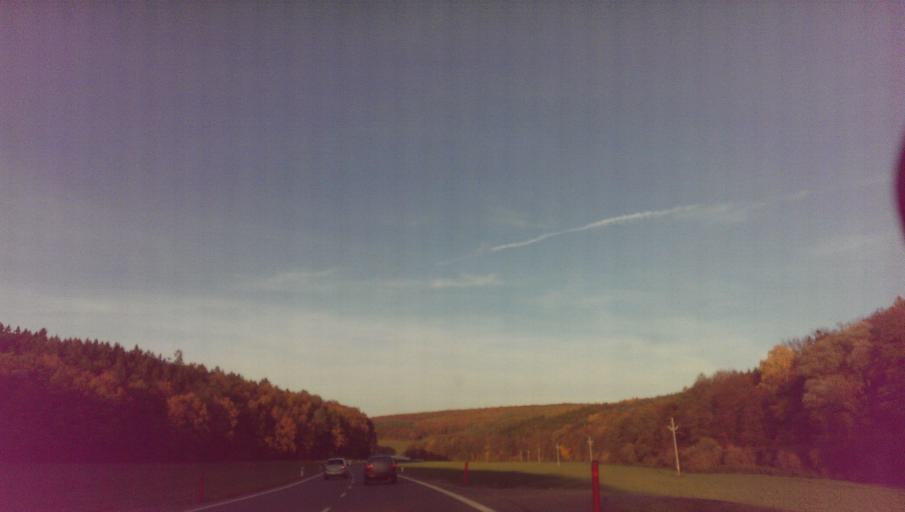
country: CZ
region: Zlin
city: Brezolupy
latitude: 49.1342
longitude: 17.5992
